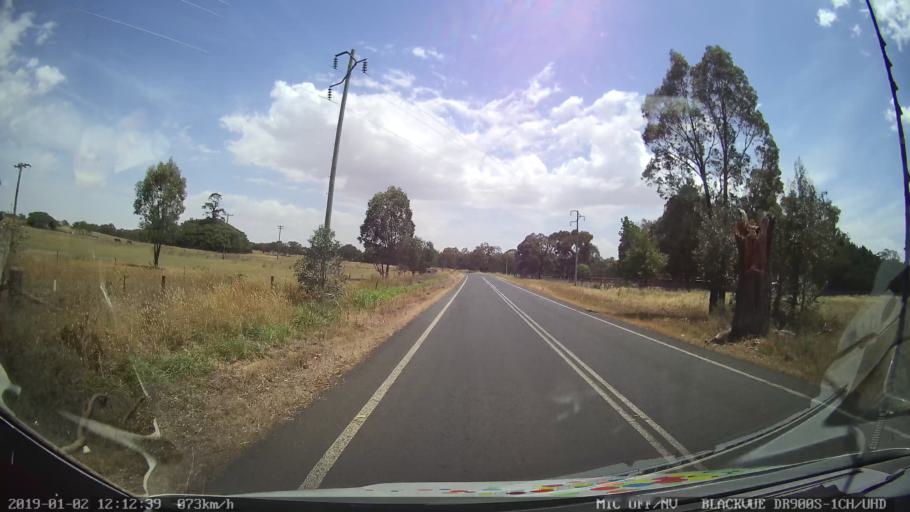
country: AU
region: New South Wales
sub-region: Young
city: Young
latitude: -34.4349
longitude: 148.2540
